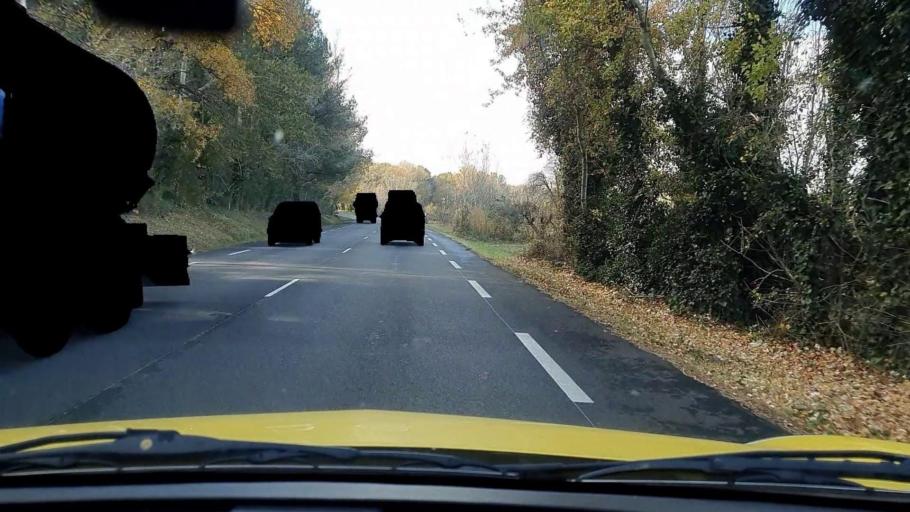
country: FR
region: Languedoc-Roussillon
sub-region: Departement du Gard
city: Vallabregues
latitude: 43.8678
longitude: 4.6229
